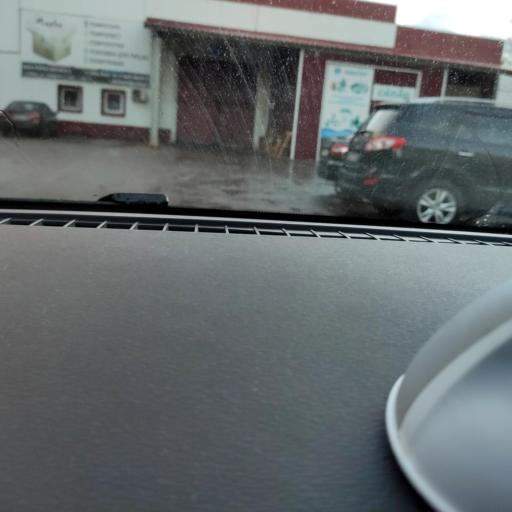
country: RU
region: Samara
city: Petra-Dubrava
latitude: 53.2330
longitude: 50.2956
